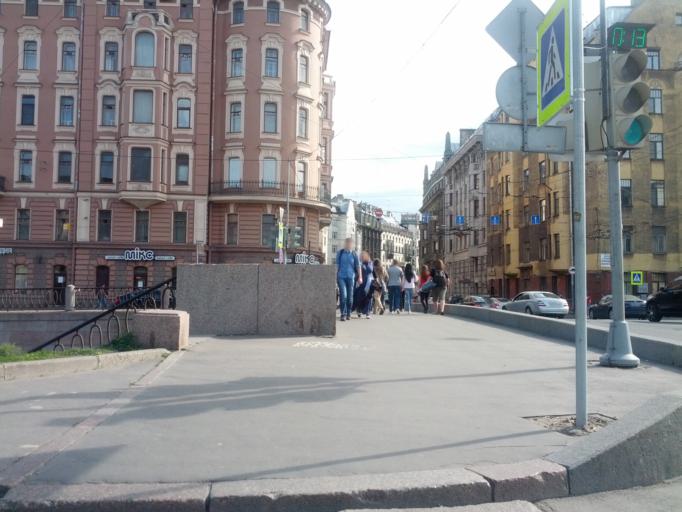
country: RU
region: St.-Petersburg
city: Petrogradka
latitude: 59.9681
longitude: 30.3144
